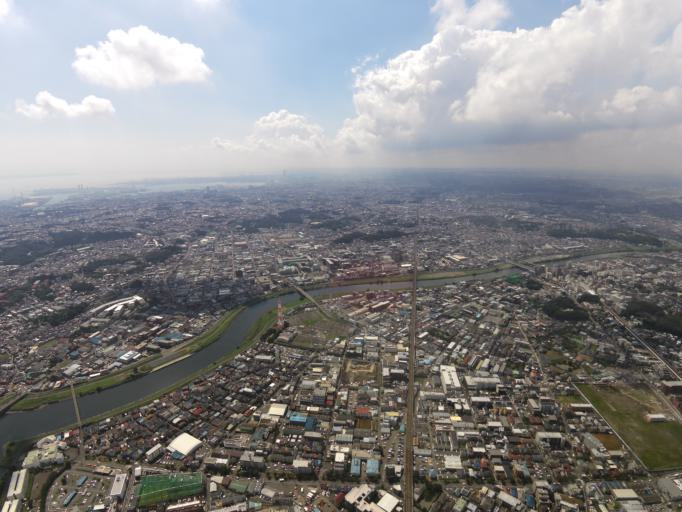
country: JP
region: Kanagawa
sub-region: Kawasaki-shi
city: Kawasaki
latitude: 35.5447
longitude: 139.6495
